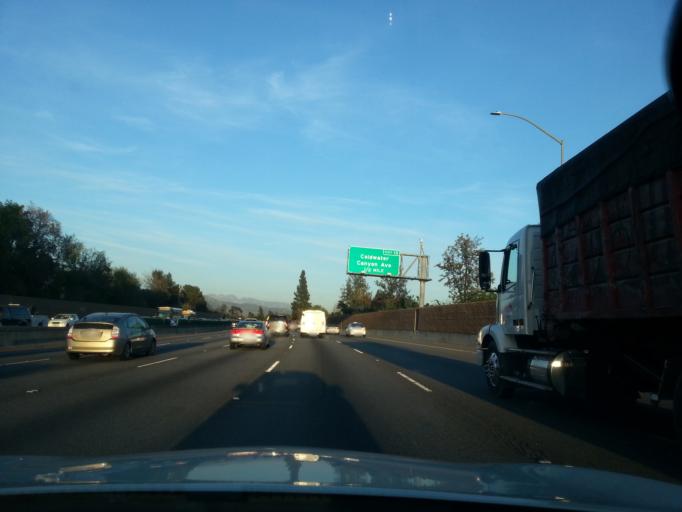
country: US
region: California
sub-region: Los Angeles County
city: Sherman Oaks
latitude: 34.1556
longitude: -118.4271
